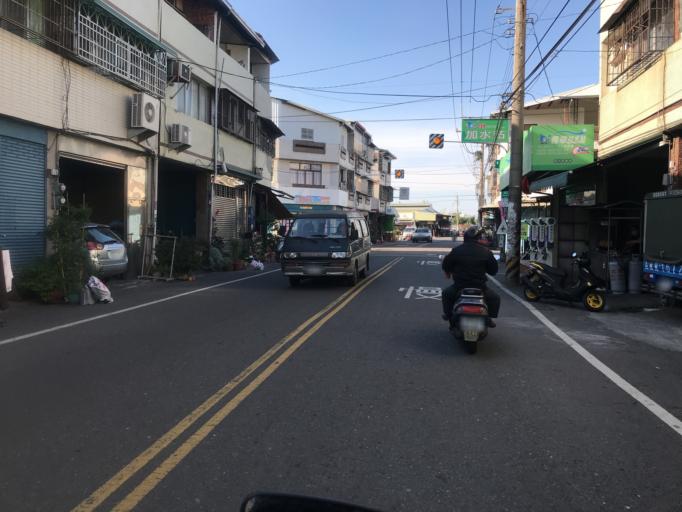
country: TW
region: Taiwan
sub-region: Nantou
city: Nantou
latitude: 23.8558
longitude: 120.5826
